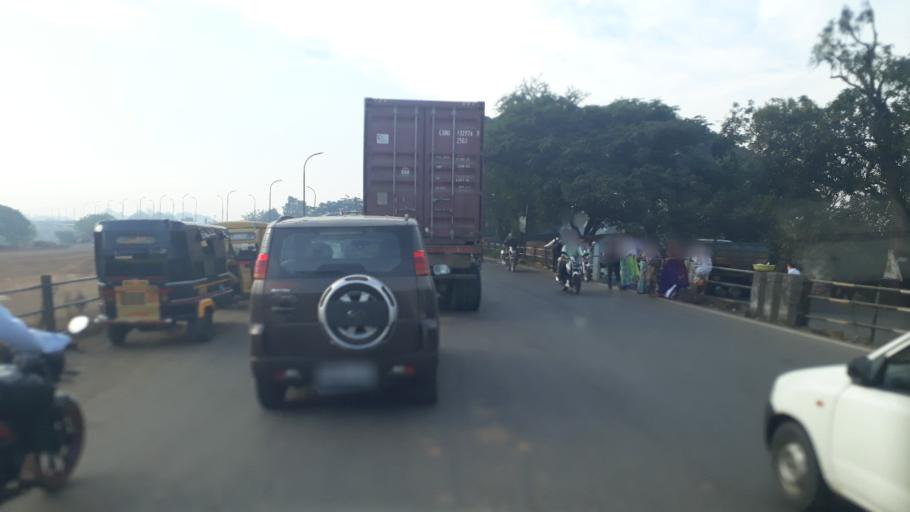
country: IN
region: Maharashtra
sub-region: Raigarh
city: Pen
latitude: 18.8427
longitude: 73.0933
